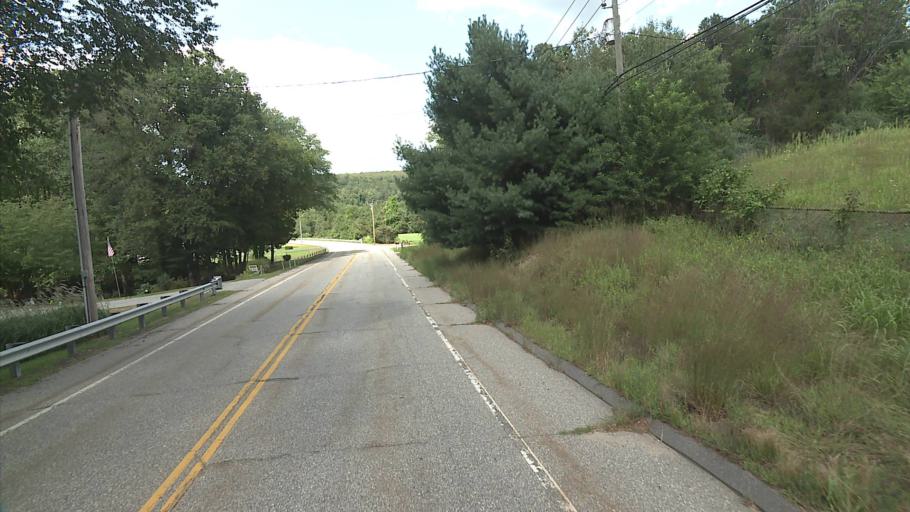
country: US
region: Connecticut
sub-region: New London County
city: Baltic
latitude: 41.6316
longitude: -72.1279
